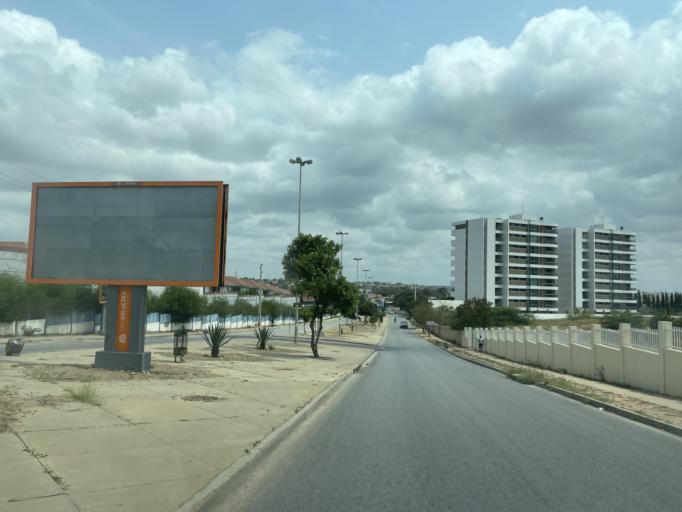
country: AO
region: Luanda
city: Luanda
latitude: -8.9244
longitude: 13.1943
